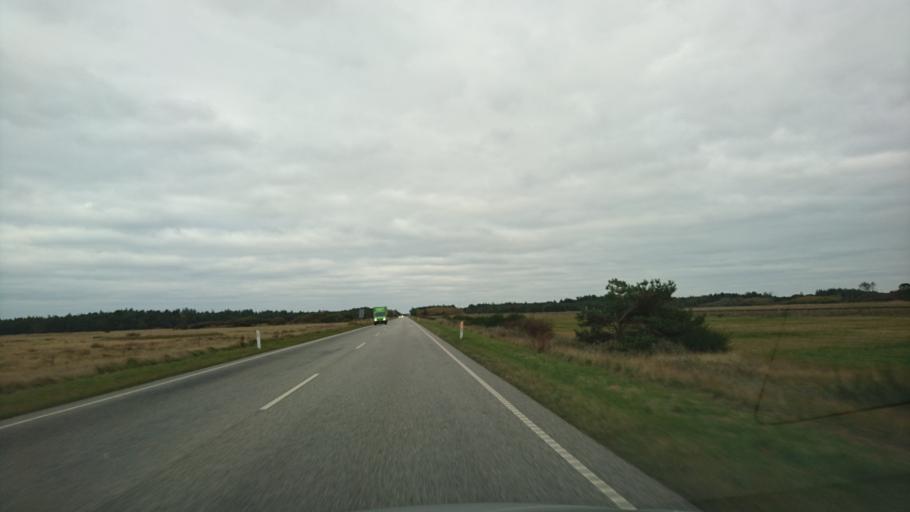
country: DK
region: North Denmark
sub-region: Frederikshavn Kommune
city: Skagen
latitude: 57.7135
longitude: 10.5272
